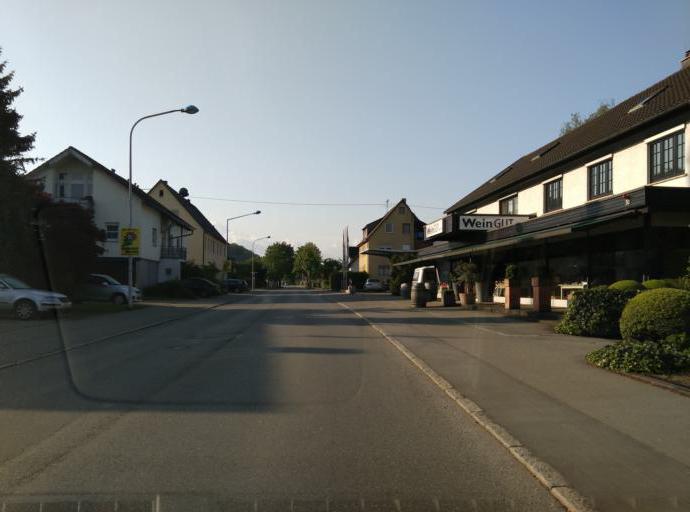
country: DE
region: Baden-Wuerttemberg
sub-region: Tuebingen Region
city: Kirchentellinsfurt
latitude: 48.5293
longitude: 9.1409
